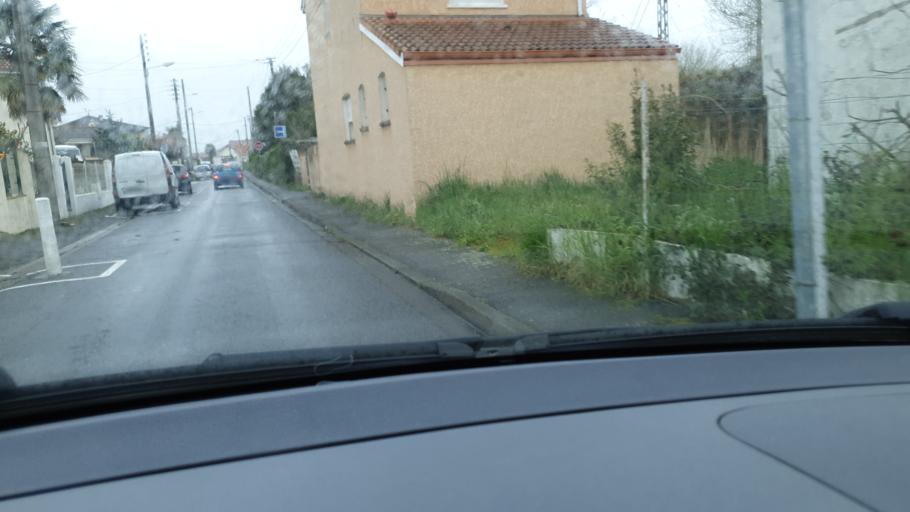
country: FR
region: Midi-Pyrenees
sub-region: Departement des Hautes-Pyrenees
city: Tarbes
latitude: 43.2414
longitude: 0.0566
